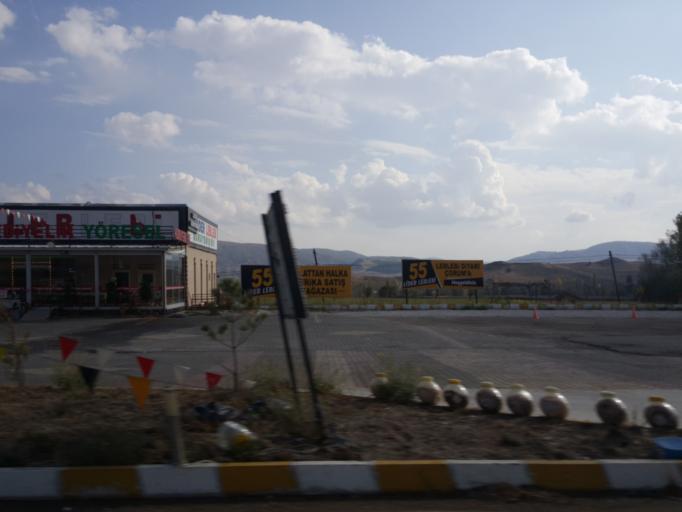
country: TR
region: Corum
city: Seydim
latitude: 40.4299
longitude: 34.7879
